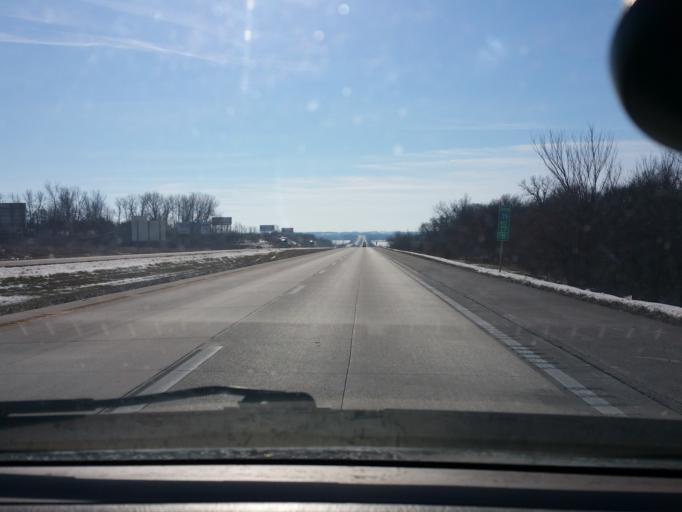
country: US
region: Missouri
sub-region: Daviess County
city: Gallatin
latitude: 40.0621
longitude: -94.0942
